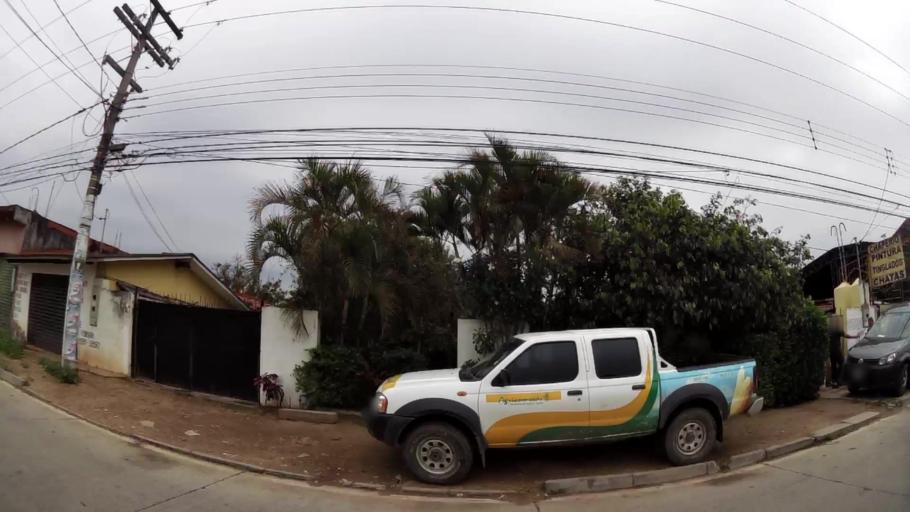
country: BO
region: Santa Cruz
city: Santa Cruz de la Sierra
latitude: -17.7757
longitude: -63.1553
